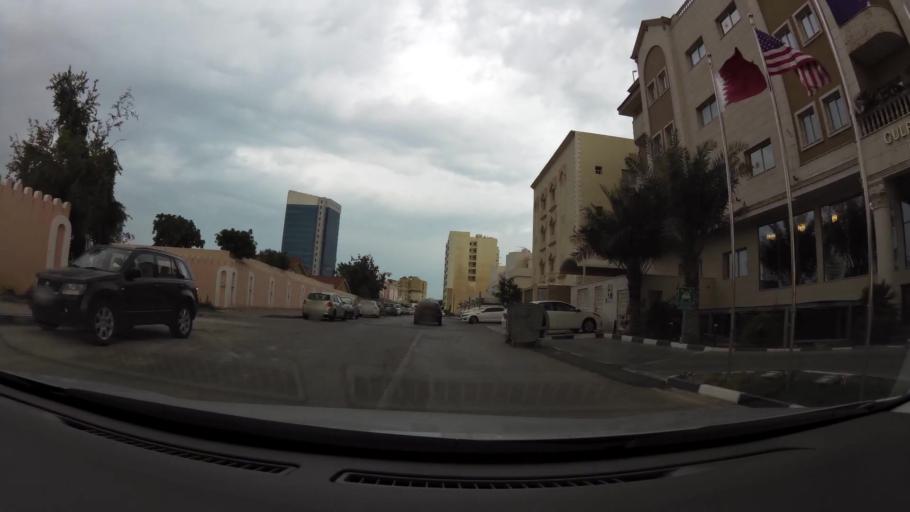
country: QA
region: Baladiyat ad Dawhah
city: Doha
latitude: 25.2728
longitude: 51.5072
